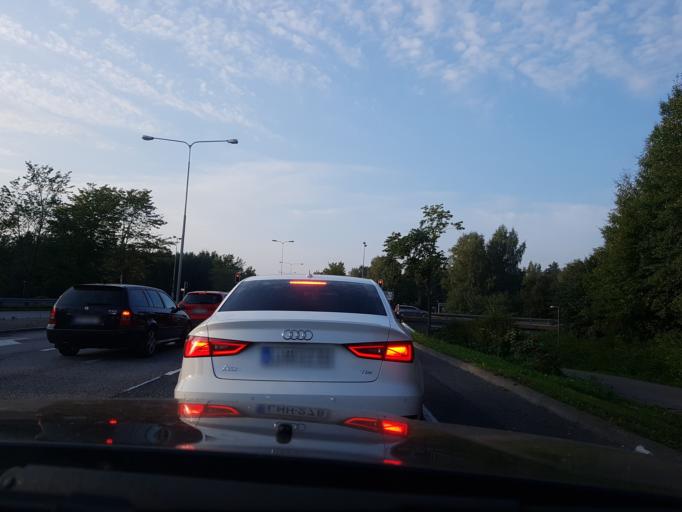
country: FI
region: Uusimaa
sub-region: Helsinki
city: Tuusula
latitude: 60.3882
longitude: 25.0250
